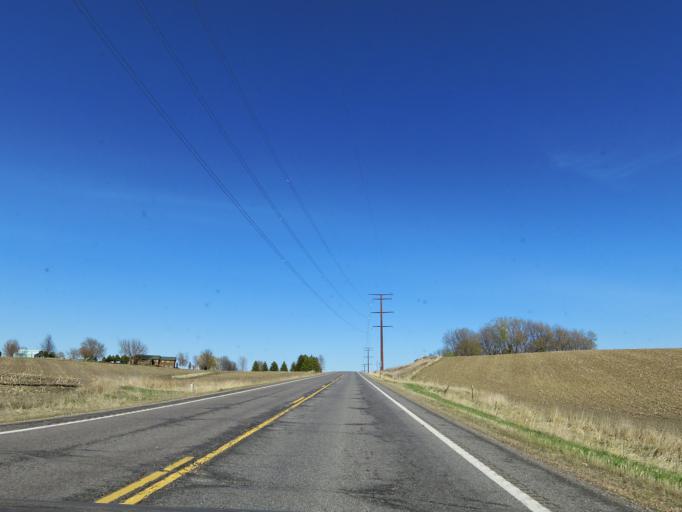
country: US
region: Minnesota
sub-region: Rice County
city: Lonsdale
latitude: 44.5728
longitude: -93.4243
